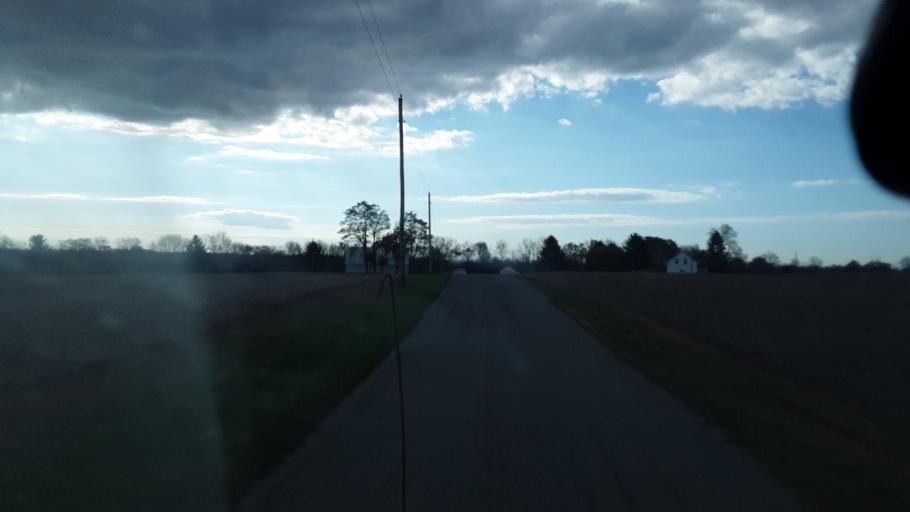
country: US
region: Ohio
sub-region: Highland County
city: Leesburg
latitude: 39.3481
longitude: -83.4750
